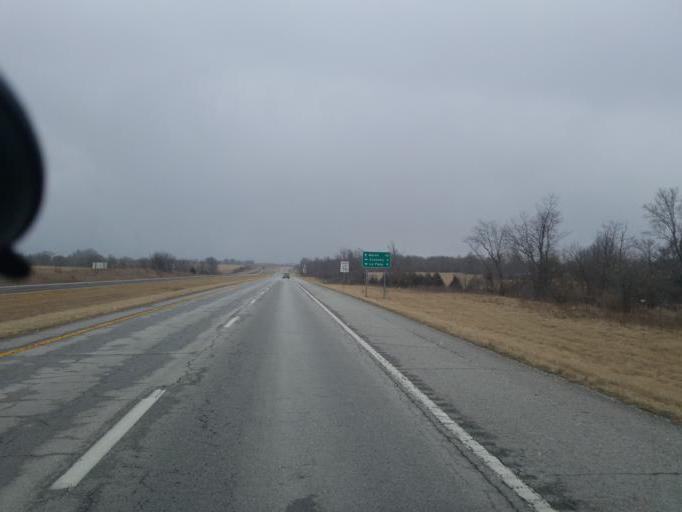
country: US
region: Missouri
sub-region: Macon County
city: La Plata
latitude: 39.8973
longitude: -92.4720
